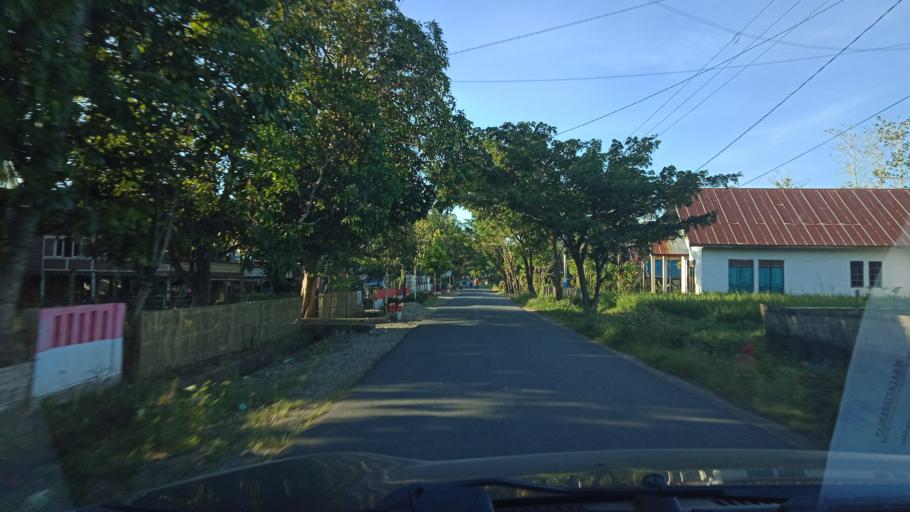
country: ID
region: South Sulawesi
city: Watampone
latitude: -4.4929
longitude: 120.3453
